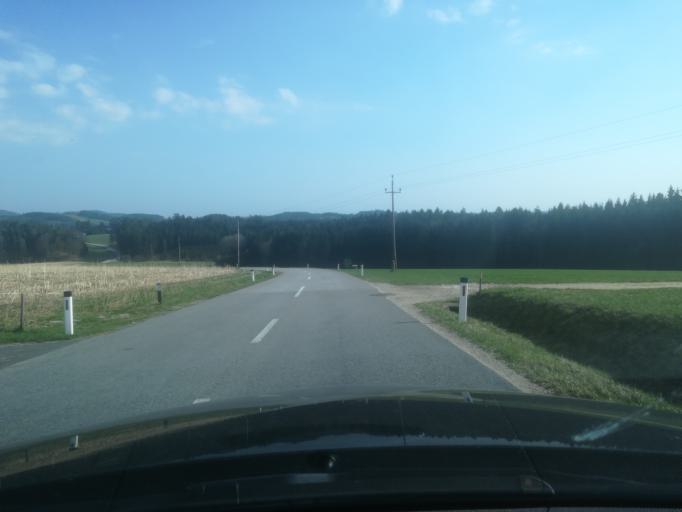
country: AT
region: Upper Austria
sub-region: Politischer Bezirk Perg
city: Perg
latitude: 48.3671
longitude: 14.6481
